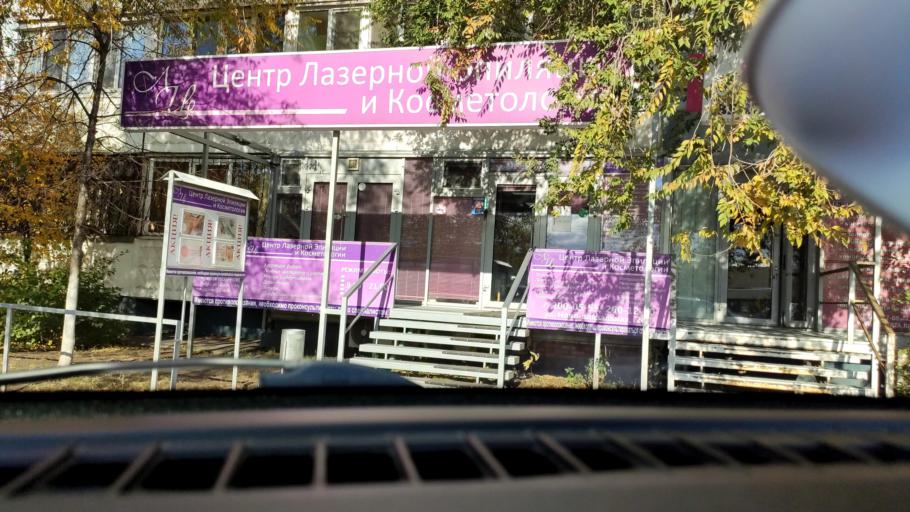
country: RU
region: Samara
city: Samara
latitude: 53.2440
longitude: 50.2091
